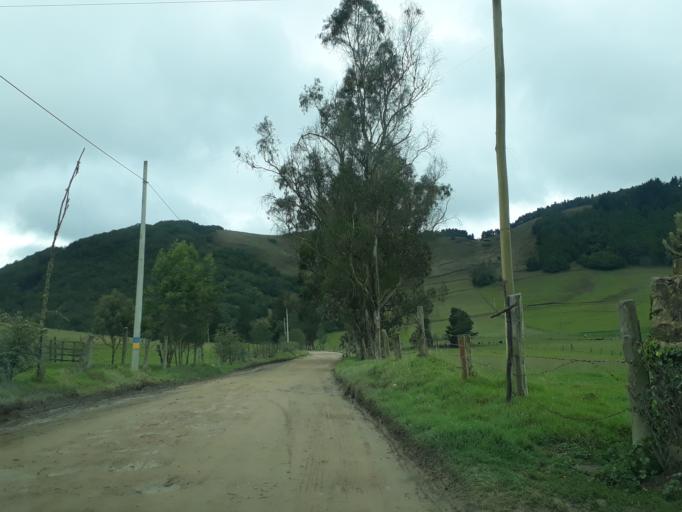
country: CO
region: Cundinamarca
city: Cucunuba
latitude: 5.2015
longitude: -73.7573
